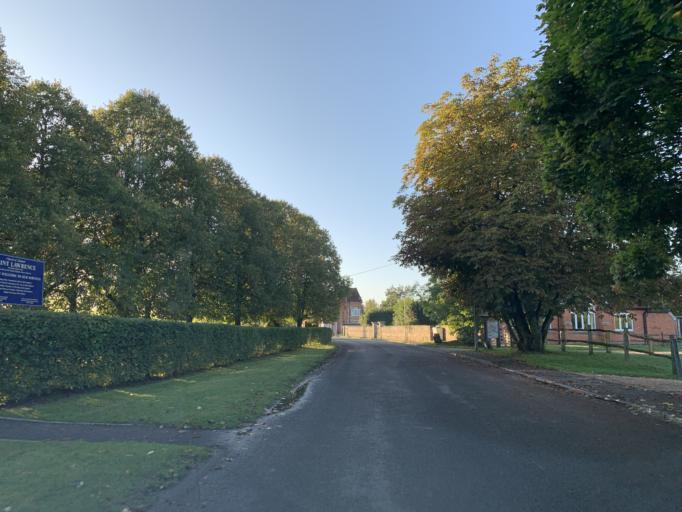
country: GB
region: England
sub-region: Wiltshire
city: Woodford
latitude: 51.0924
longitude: -1.8156
